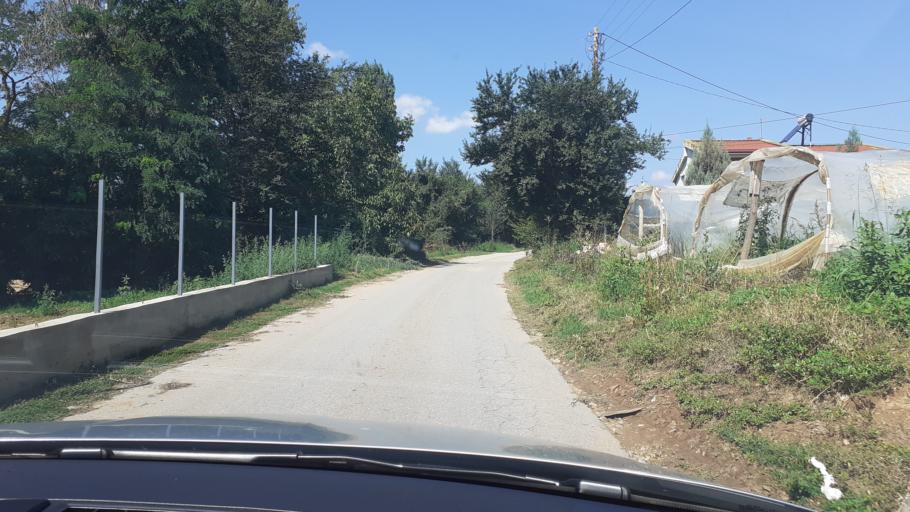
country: MK
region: Vasilevo
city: Vasilevo
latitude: 41.5187
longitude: 22.6060
